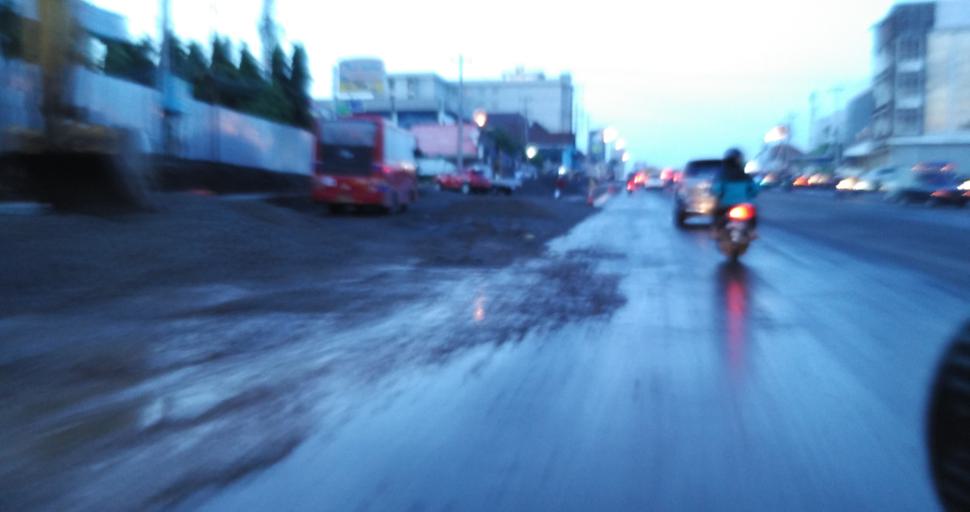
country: ID
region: Central Java
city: Semarang
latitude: -7.0300
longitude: 110.4182
